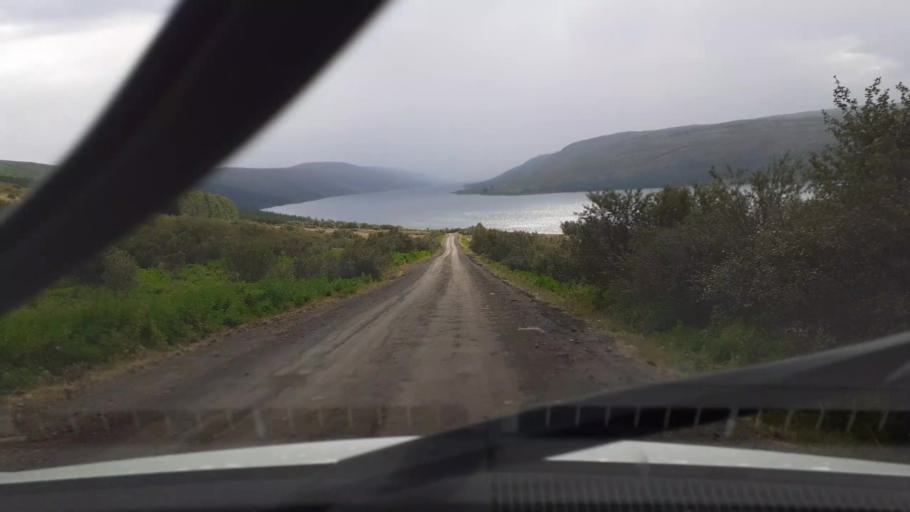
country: IS
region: Capital Region
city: Mosfellsbaer
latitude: 64.5246
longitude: -21.4762
